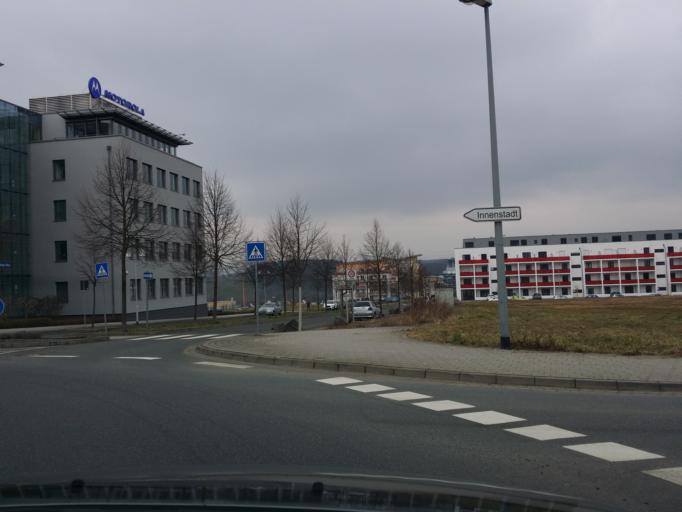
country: DE
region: Hesse
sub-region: Regierungsbezirk Darmstadt
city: Idstein
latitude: 50.2239
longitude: 8.2578
